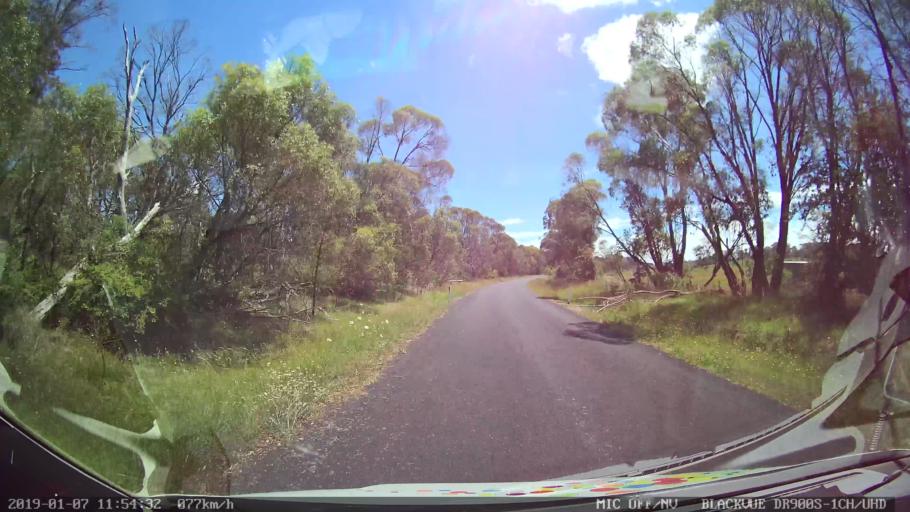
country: AU
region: New South Wales
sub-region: Guyra
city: Guyra
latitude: -30.2949
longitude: 151.6644
